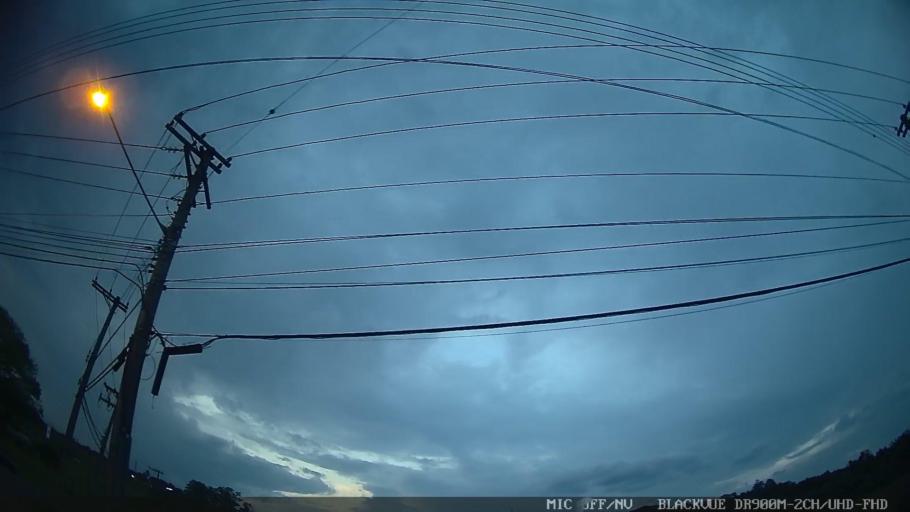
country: BR
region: Sao Paulo
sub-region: Louveira
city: Louveira
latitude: -23.1324
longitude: -46.9758
